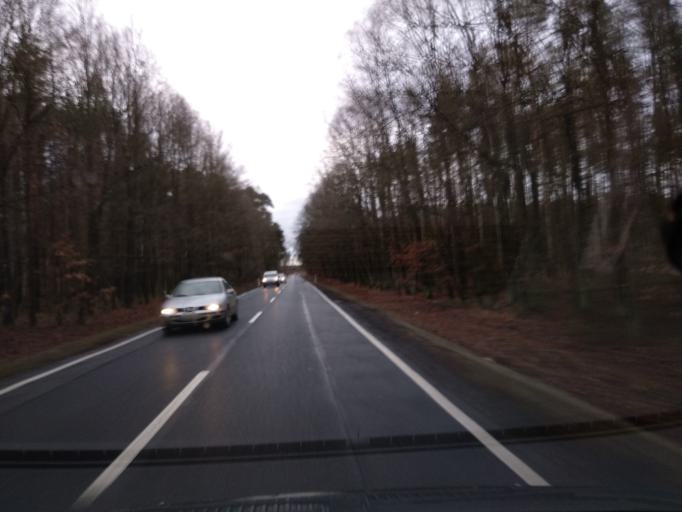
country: PL
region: Lower Silesian Voivodeship
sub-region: Powiat olesnicki
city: Olesnica
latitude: 51.2571
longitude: 17.4795
